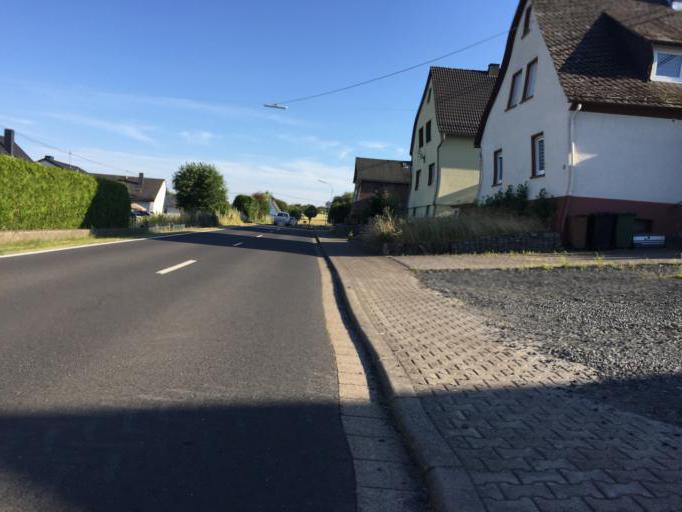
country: DE
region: Rheinland-Pfalz
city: Kaden
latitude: 50.5463
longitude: 7.9135
